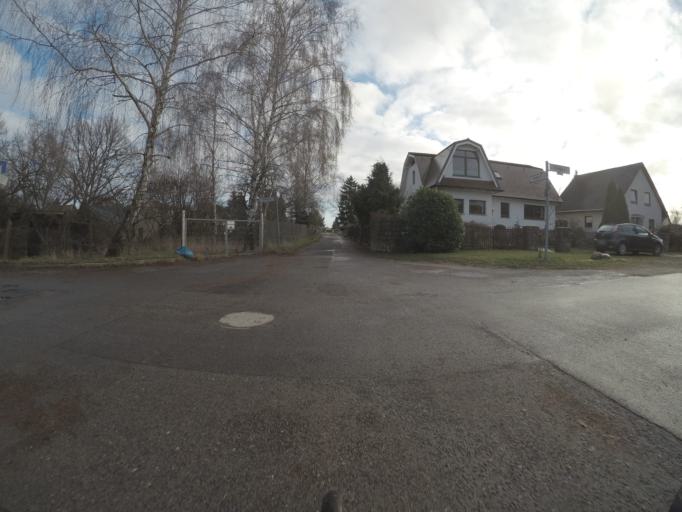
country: DE
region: Berlin
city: Wartenberg
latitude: 52.5879
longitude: 13.5343
